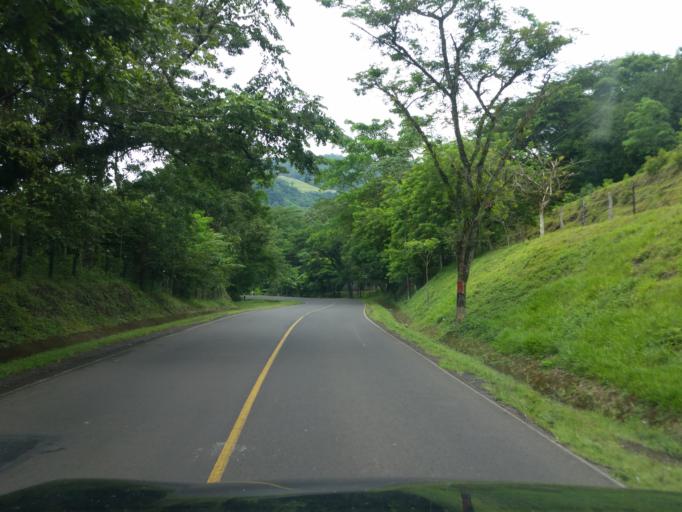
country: NI
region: Matagalpa
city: San Ramon
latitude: 13.0491
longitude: -85.7658
